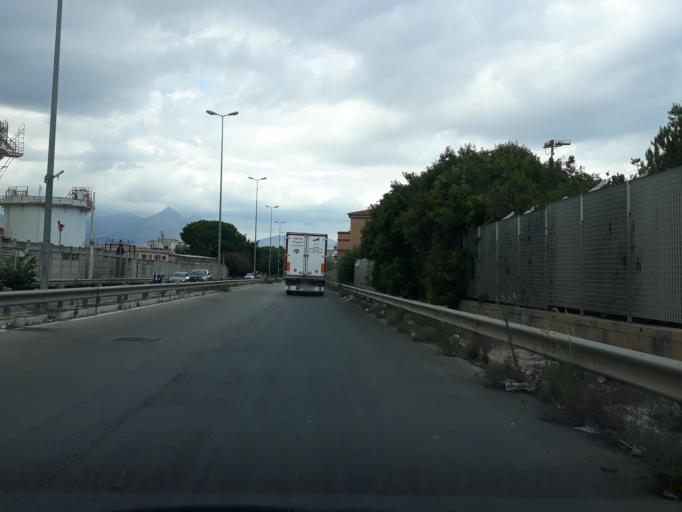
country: IT
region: Sicily
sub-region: Palermo
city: Ciaculli
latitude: 38.0930
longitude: 13.4059
